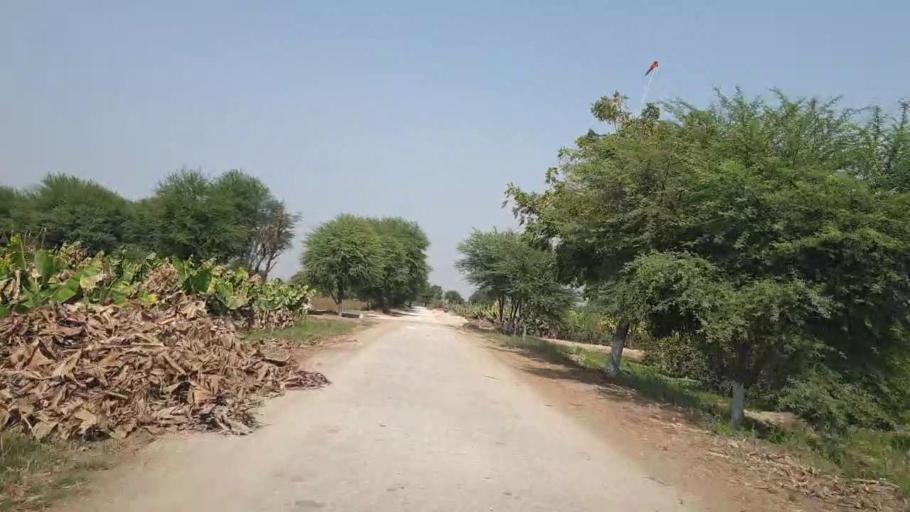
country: PK
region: Sindh
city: Dhoro Naro
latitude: 25.4907
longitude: 69.6288
